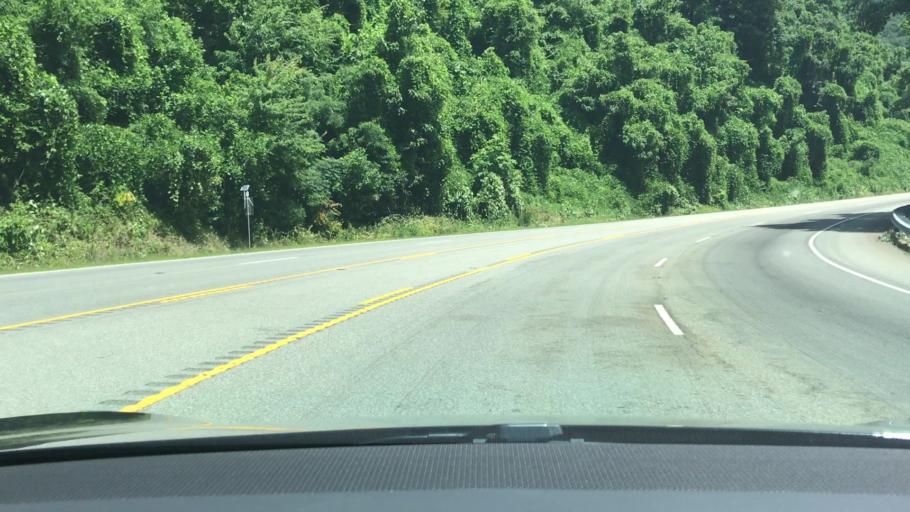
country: US
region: North Carolina
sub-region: Macon County
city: Franklin
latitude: 35.2546
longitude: -83.3174
